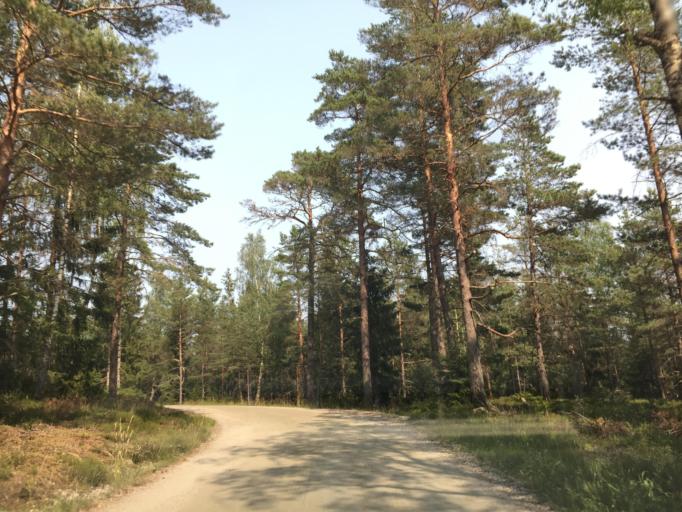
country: SE
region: Vaestra Goetaland
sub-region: Lilla Edets Kommun
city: Lilla Edet
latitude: 58.2468
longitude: 12.0874
